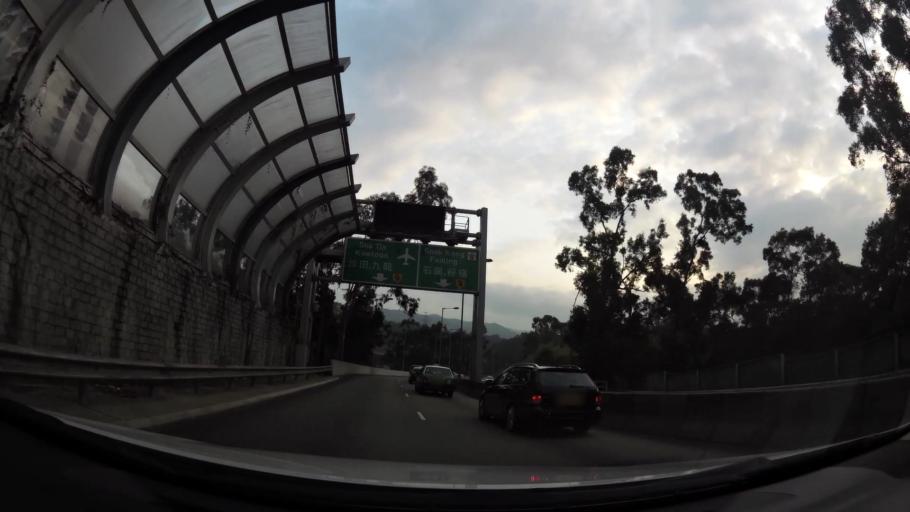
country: HK
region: Tai Po
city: Tai Po
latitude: 22.4510
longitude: 114.1584
